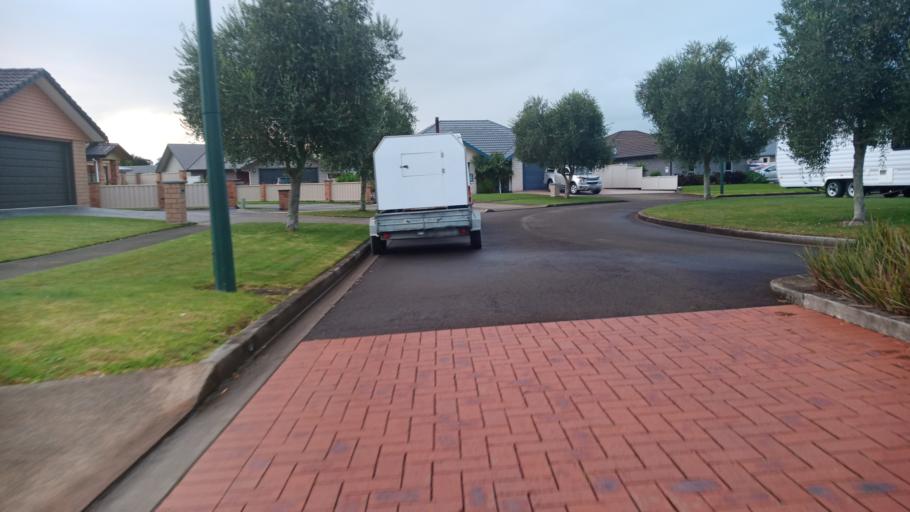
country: NZ
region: Gisborne
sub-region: Gisborne District
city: Gisborne
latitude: -38.6376
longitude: 177.9990
